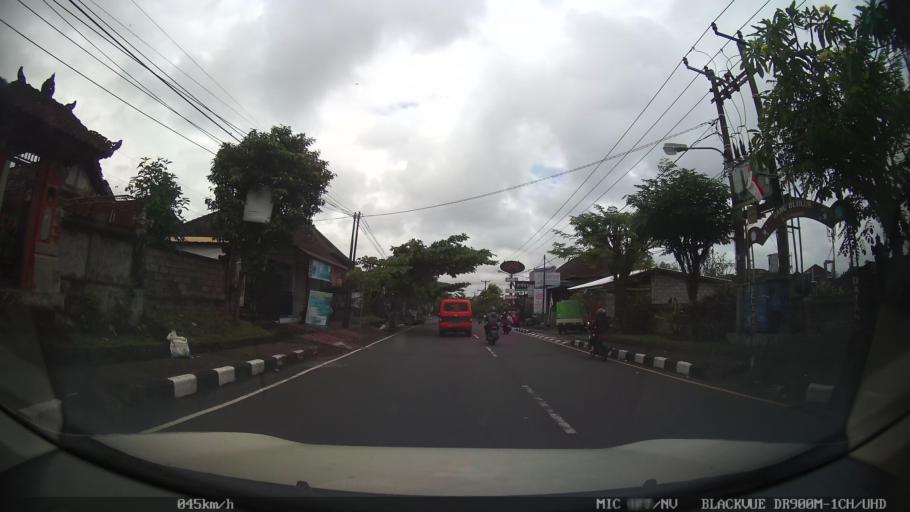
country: ID
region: Bali
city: Banjar Serangan
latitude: -8.5388
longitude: 115.1707
